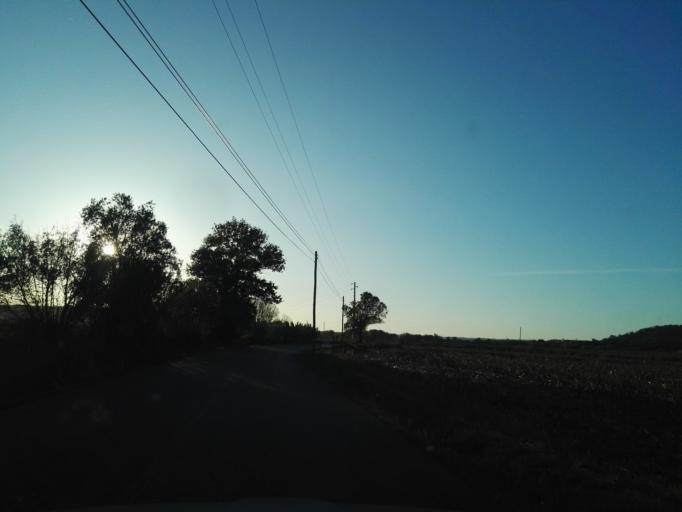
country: PT
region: Santarem
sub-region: Alpiarca
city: Alpiarca
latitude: 39.3397
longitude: -8.5694
